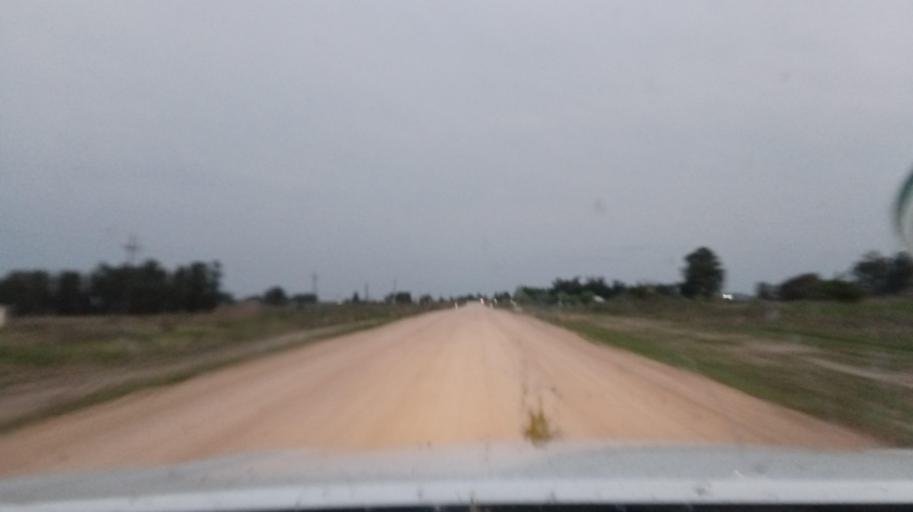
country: UY
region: Canelones
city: Santa Rosa
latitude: -34.5343
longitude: -56.0993
